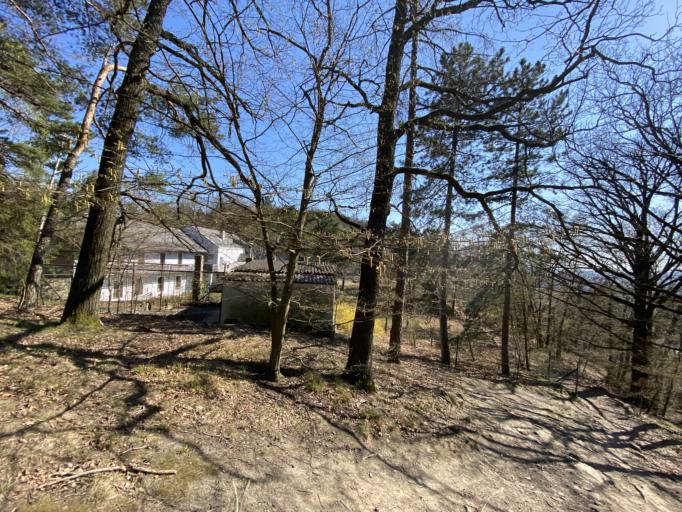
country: AT
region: Lower Austria
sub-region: Politischer Bezirk Krems
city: Durnstein
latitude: 48.4074
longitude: 15.5286
